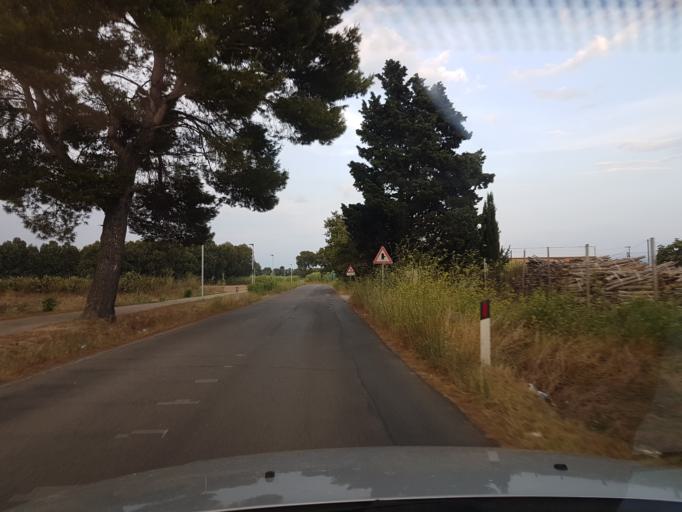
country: IT
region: Sardinia
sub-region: Provincia di Oristano
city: Cabras
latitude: 39.9293
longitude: 8.5404
